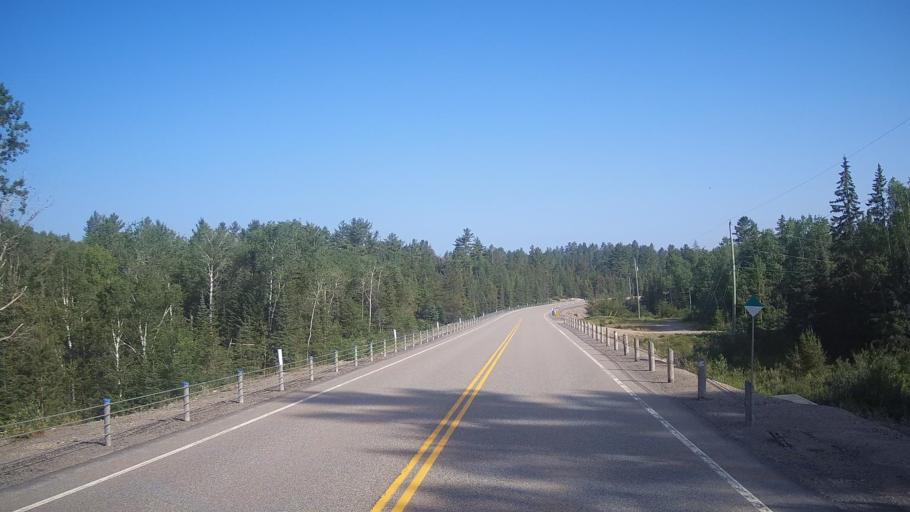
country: CA
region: Ontario
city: Rayside-Balfour
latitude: 46.7435
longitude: -81.5992
